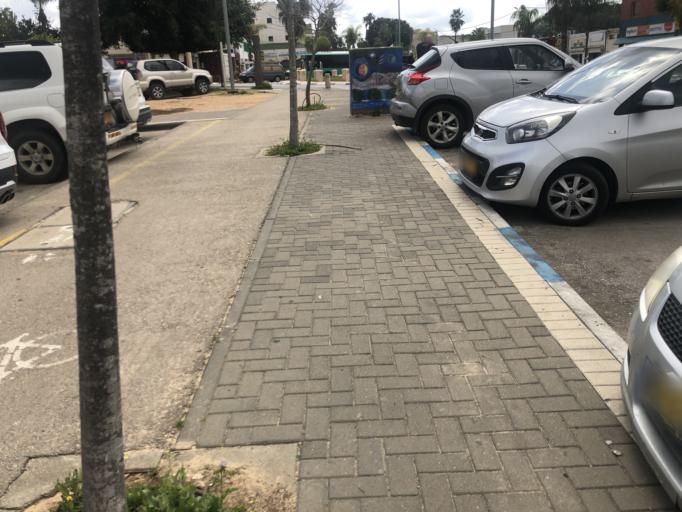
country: IL
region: Haifa
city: Hadera
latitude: 32.4753
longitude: 34.9726
